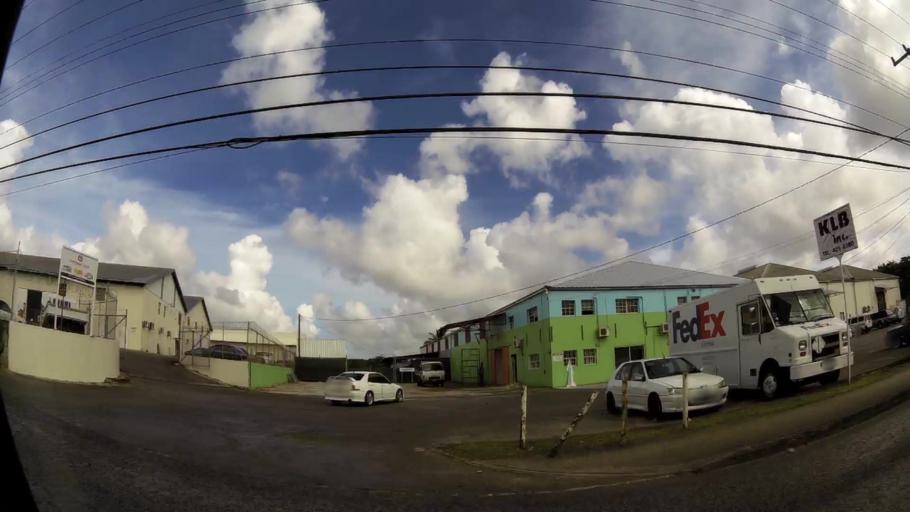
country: BB
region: Saint Michael
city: Bridgetown
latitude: 13.1323
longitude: -59.6058
